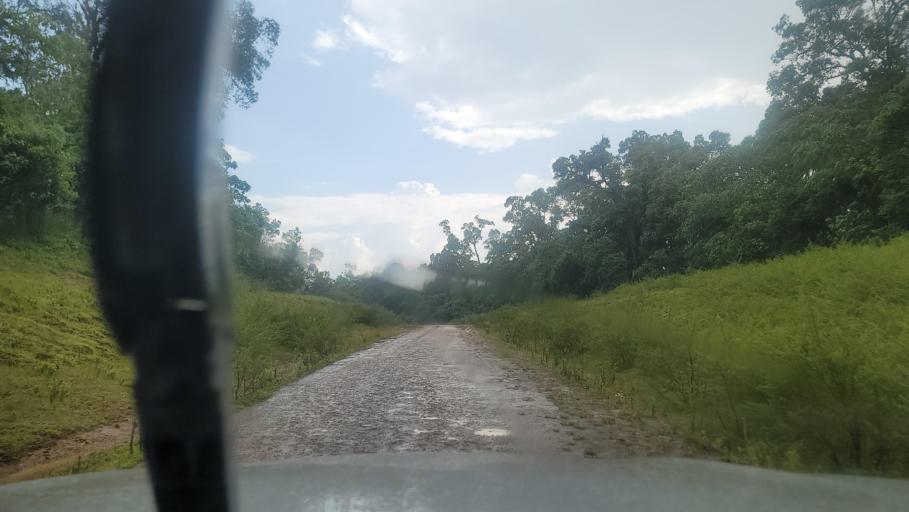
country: ET
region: Southern Nations, Nationalities, and People's Region
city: Bonga
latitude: 7.6683
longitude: 36.2433
